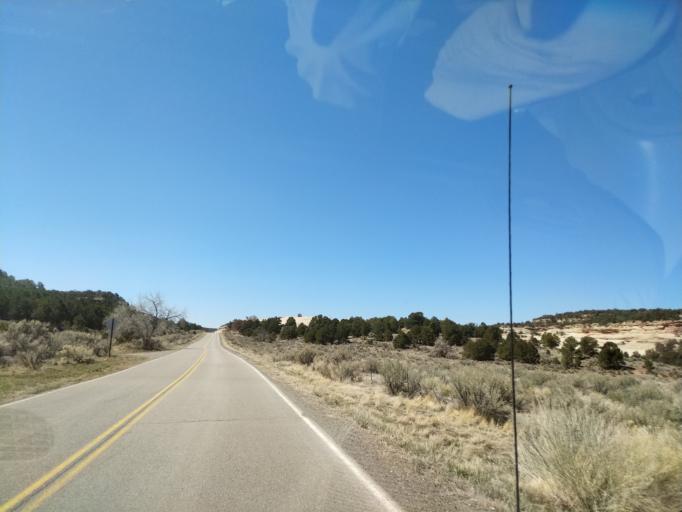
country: US
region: Colorado
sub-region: Mesa County
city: Redlands
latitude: 38.9893
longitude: -108.7860
